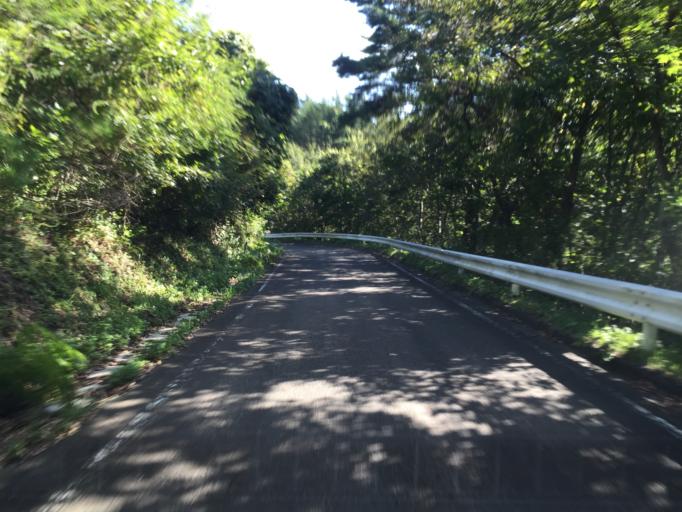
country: JP
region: Fukushima
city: Yanagawamachi-saiwaicho
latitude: 37.8348
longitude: 140.7001
